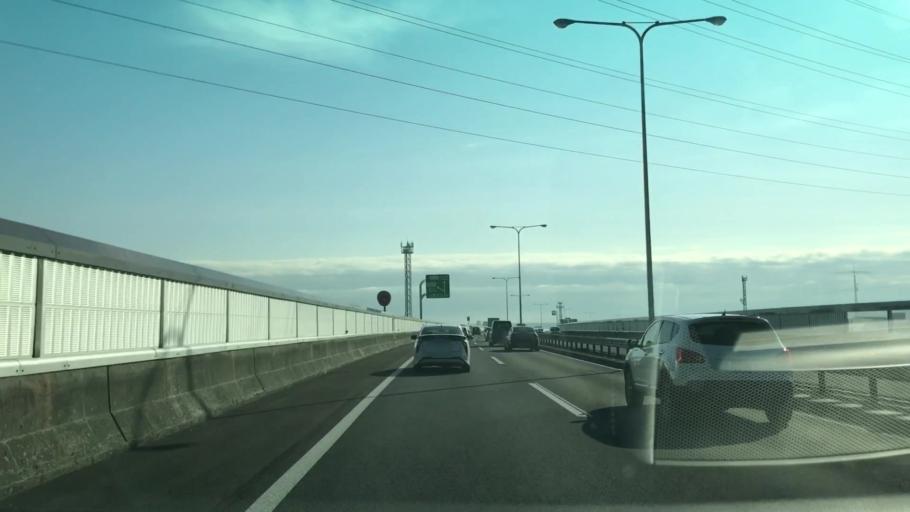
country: JP
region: Hokkaido
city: Sapporo
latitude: 43.0905
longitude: 141.4106
